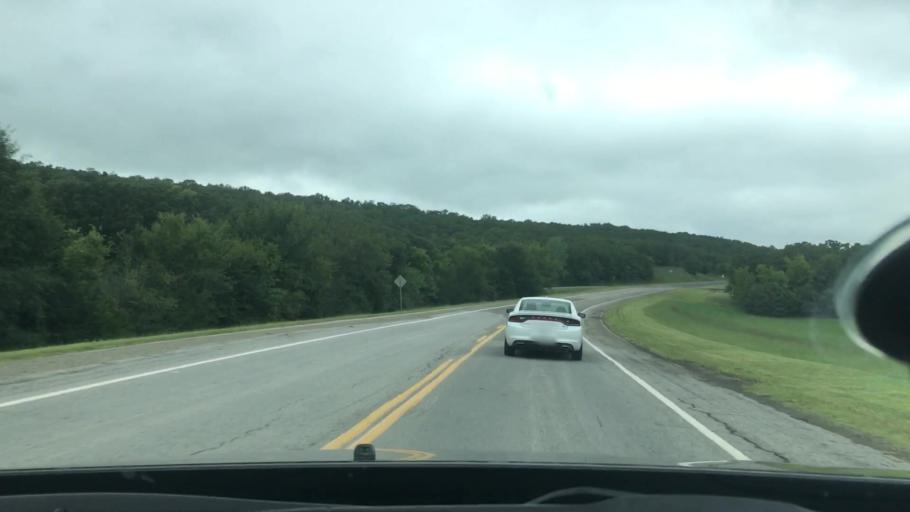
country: US
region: Oklahoma
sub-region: Sequoyah County
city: Vian
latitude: 35.5162
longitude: -94.9716
